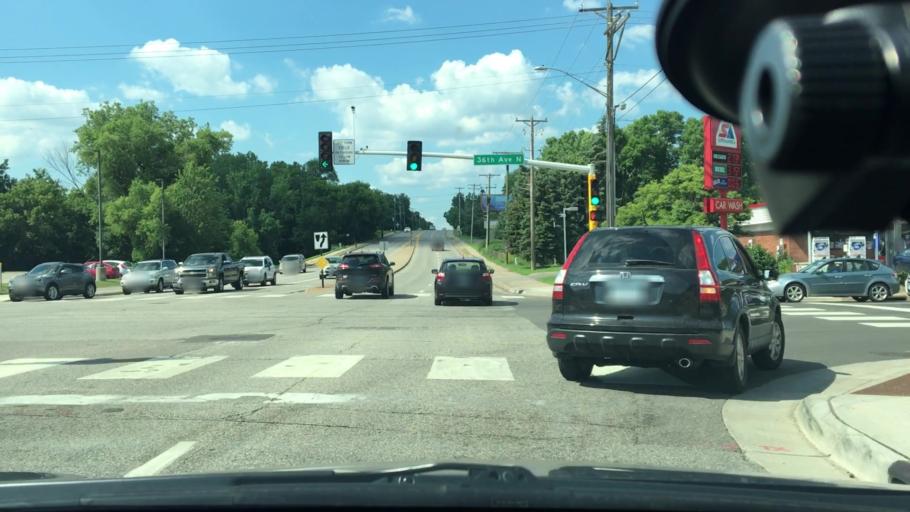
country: US
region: Minnesota
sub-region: Hennepin County
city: New Hope
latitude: 45.0217
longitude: -93.3801
